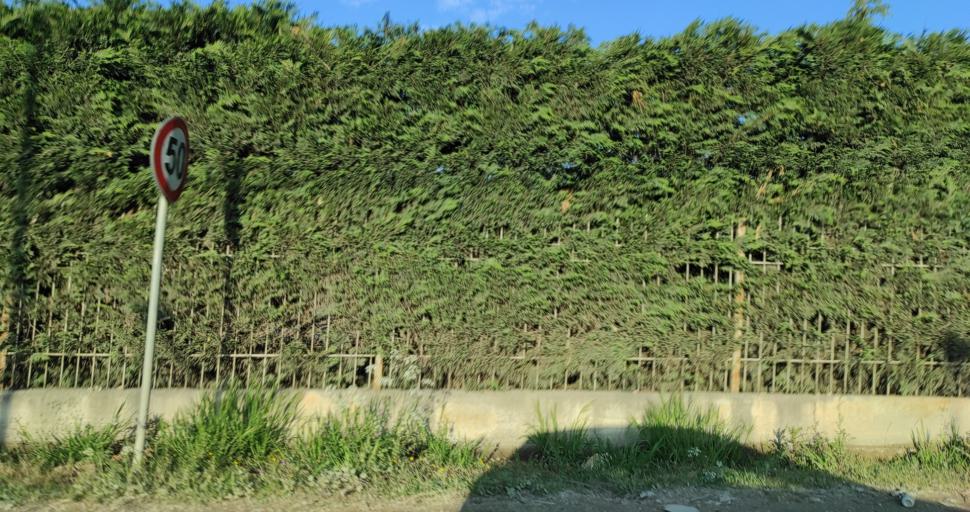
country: AL
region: Durres
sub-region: Rrethi i Krujes
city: Fushe-Kruje
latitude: 41.4786
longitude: 19.7348
